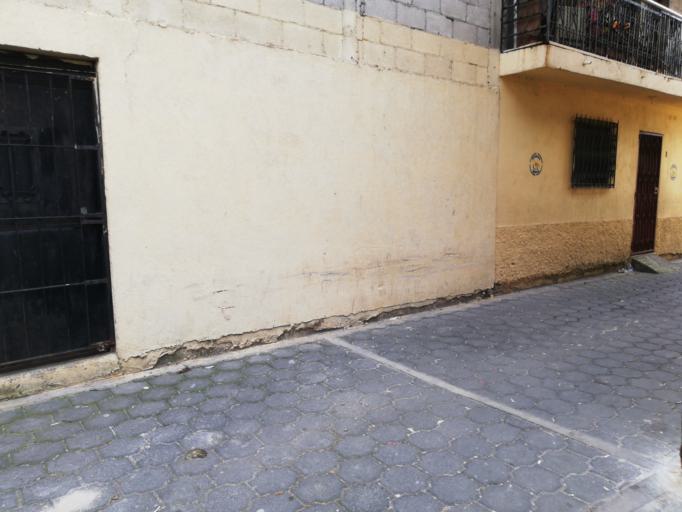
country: GT
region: Guatemala
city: Villa Nueva
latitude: 14.5711
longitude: -90.5655
